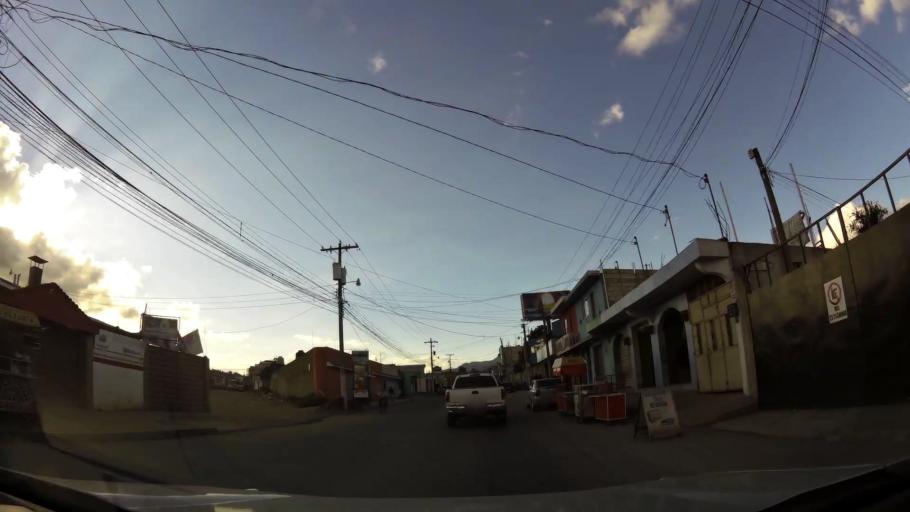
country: GT
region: Quetzaltenango
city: Quetzaltenango
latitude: 14.8524
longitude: -91.5327
